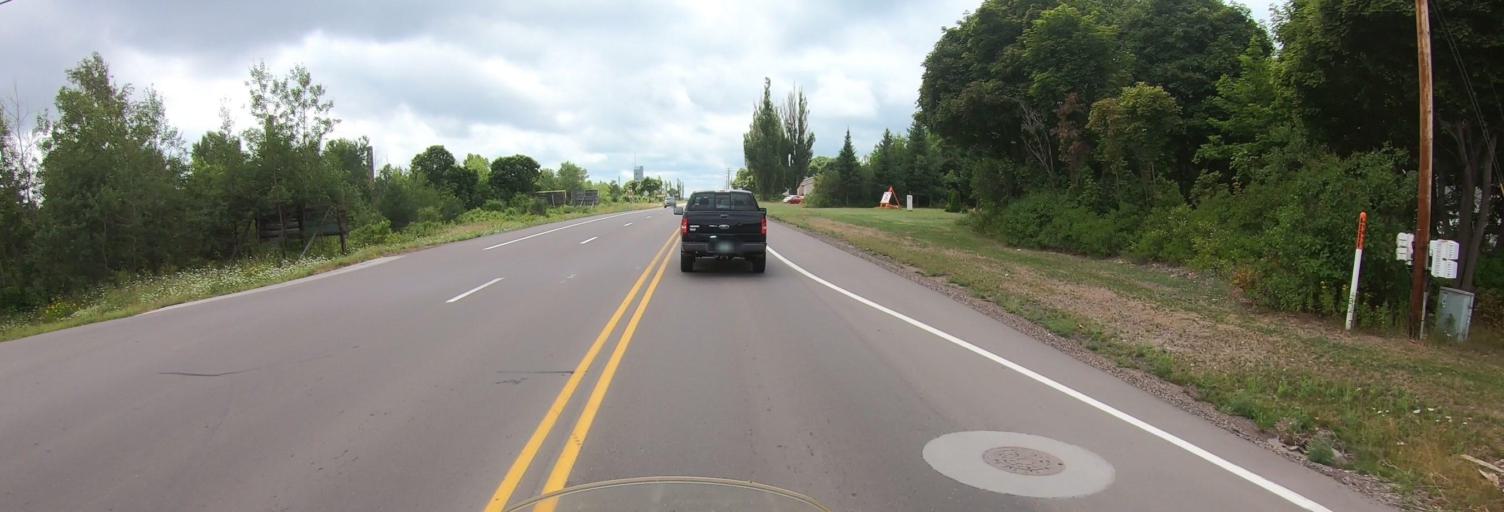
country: US
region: Michigan
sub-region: Houghton County
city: Hancock
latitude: 47.1428
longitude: -88.5702
